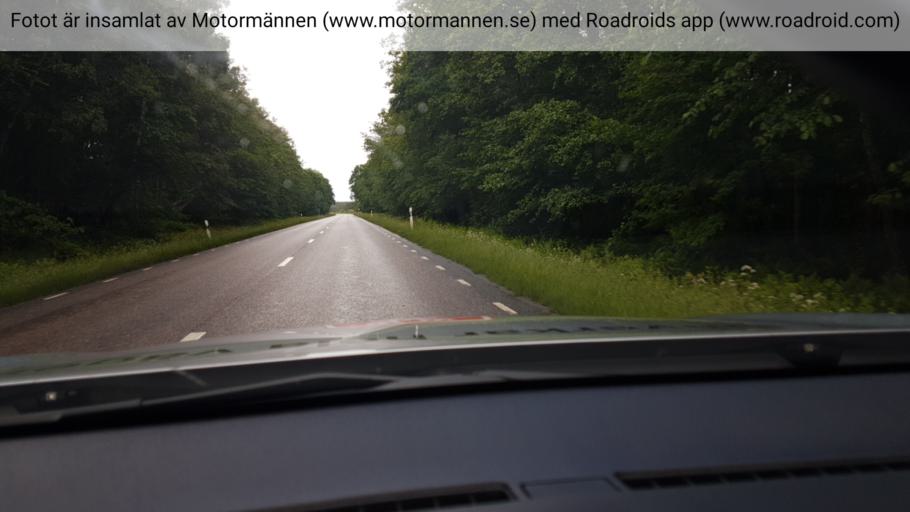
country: SE
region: Vaestra Goetaland
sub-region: Hjo Kommun
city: Hjo
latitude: 58.2341
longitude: 14.2204
